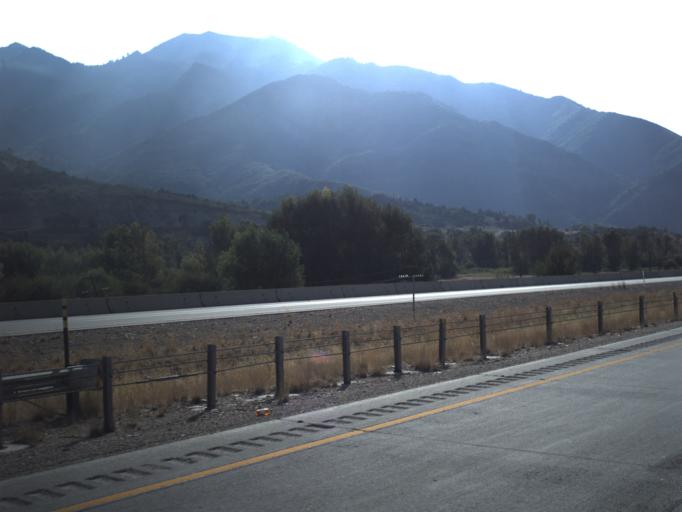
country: US
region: Utah
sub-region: Morgan County
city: Mountain Green
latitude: 41.1384
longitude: -111.8067
